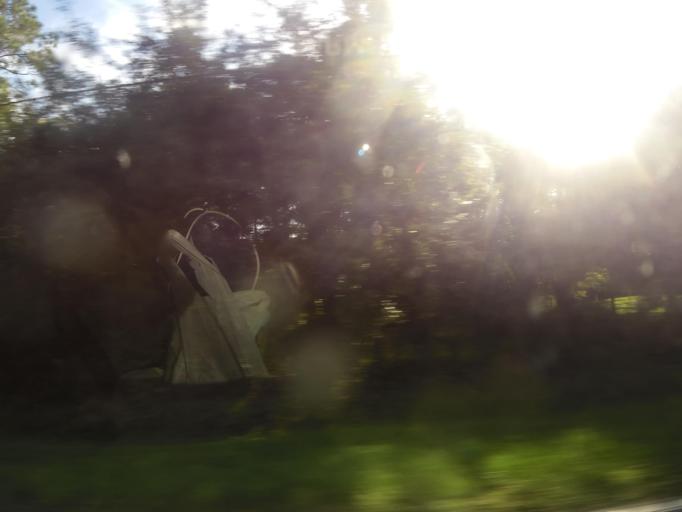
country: US
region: Florida
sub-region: Clay County
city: Green Cove Springs
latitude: 29.9179
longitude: -81.5433
